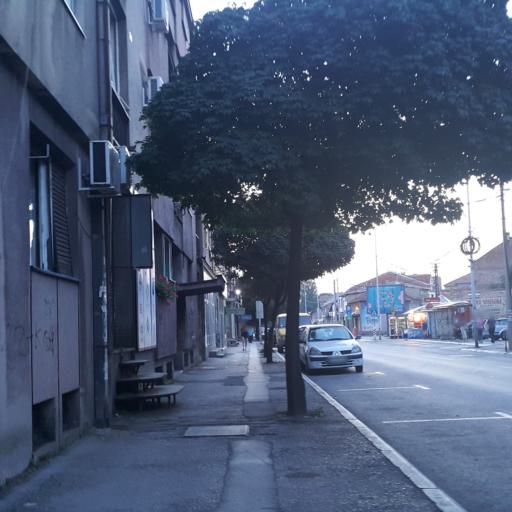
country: RS
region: Central Serbia
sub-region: Nisavski Okrug
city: Nis
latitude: 43.3160
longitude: 21.8878
